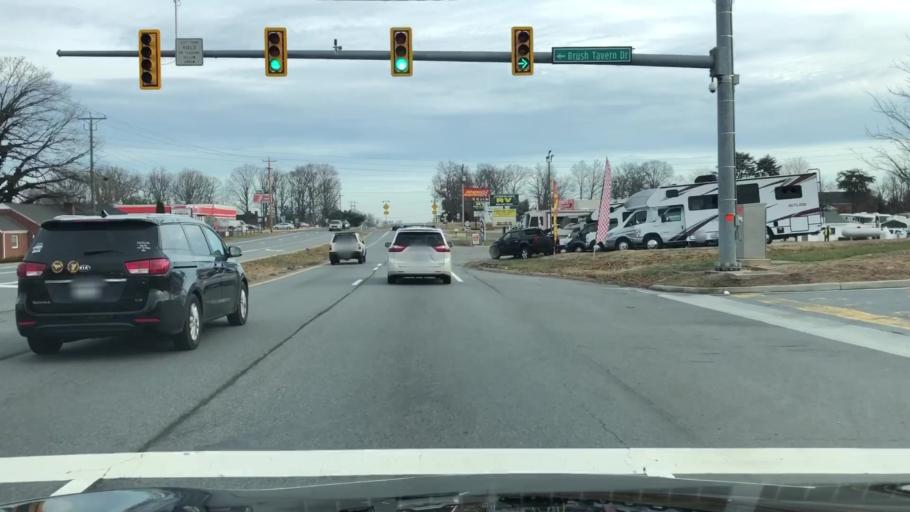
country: US
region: Virginia
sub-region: Campbell County
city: Timberlake
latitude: 37.3303
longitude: -79.2454
